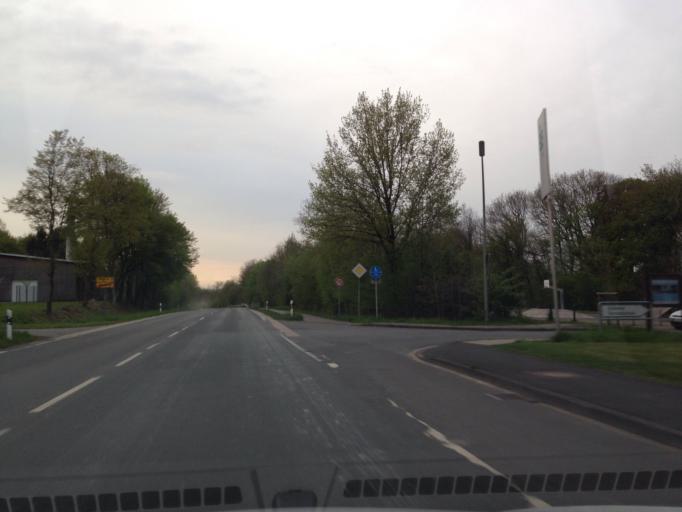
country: DE
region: North Rhine-Westphalia
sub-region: Regierungsbezirk Munster
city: Altenberge
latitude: 52.0491
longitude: 7.4653
